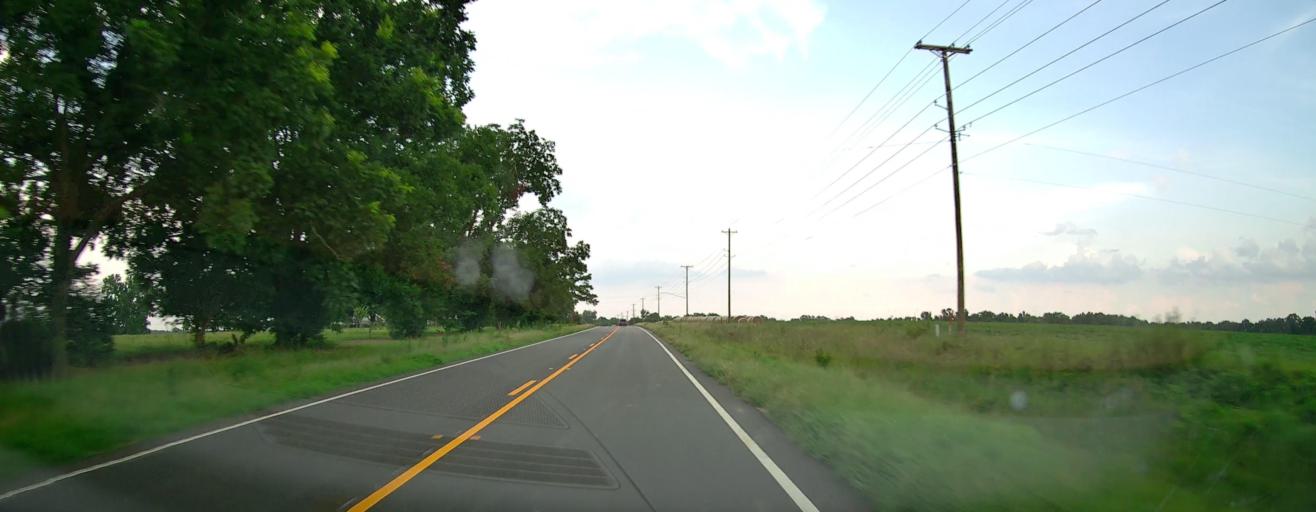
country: US
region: Georgia
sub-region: Dodge County
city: Chester
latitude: 32.5449
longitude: -83.0890
